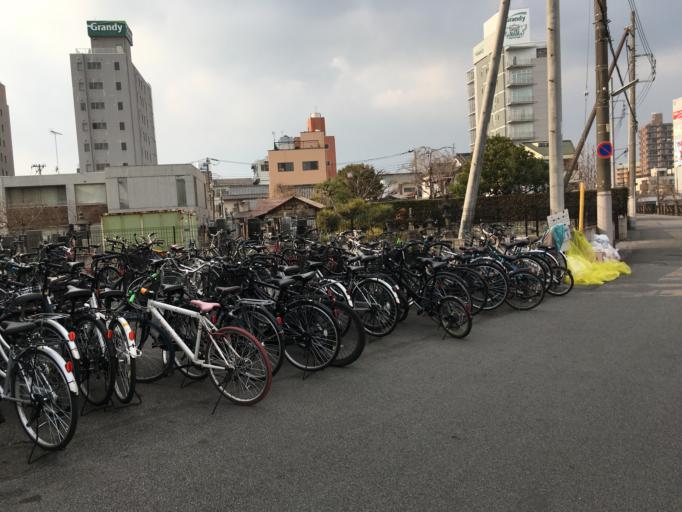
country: JP
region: Tochigi
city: Utsunomiya-shi
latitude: 36.5602
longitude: 139.8959
